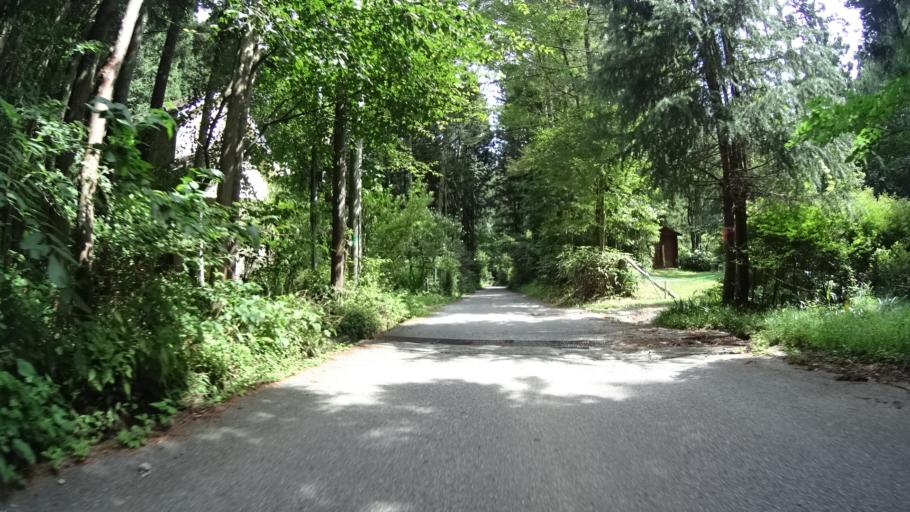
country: JP
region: Yamanashi
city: Nirasaki
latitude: 35.7884
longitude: 138.5315
